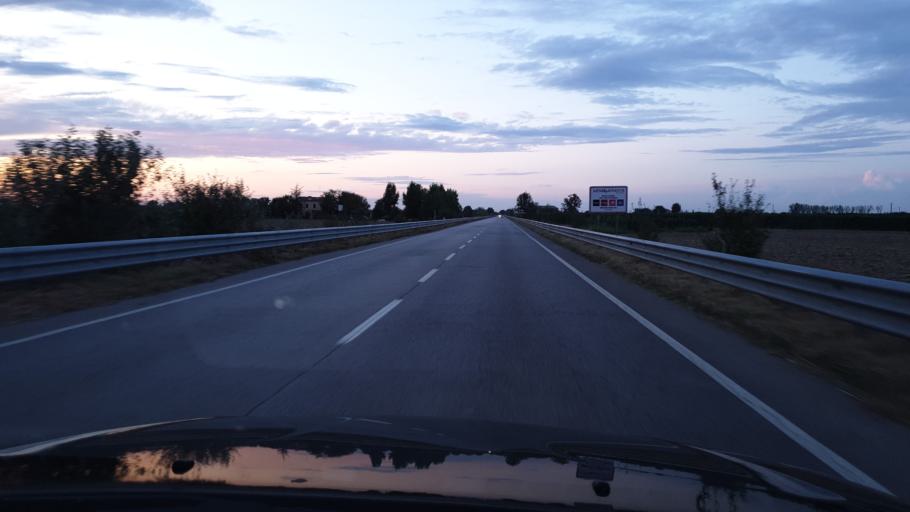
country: IT
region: Emilia-Romagna
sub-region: Provincia di Ravenna
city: Alfonsine
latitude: 44.5120
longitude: 12.0584
